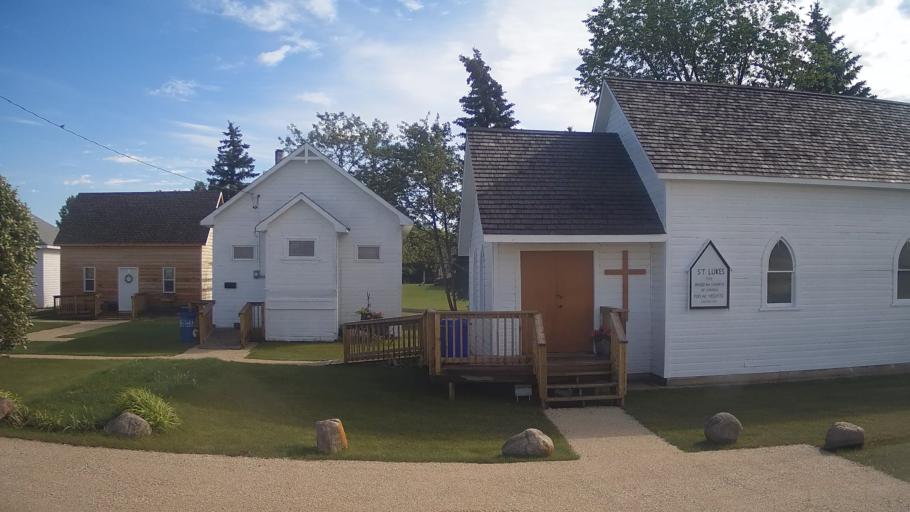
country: CA
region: Manitoba
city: Stonewall
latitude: 50.2034
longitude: -97.6552
